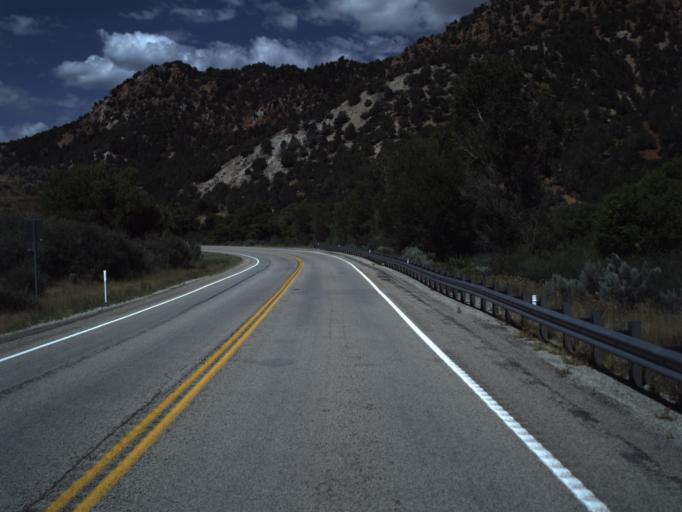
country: US
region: Utah
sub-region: Utah County
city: Woodland Hills
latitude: 39.9663
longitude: -111.5159
